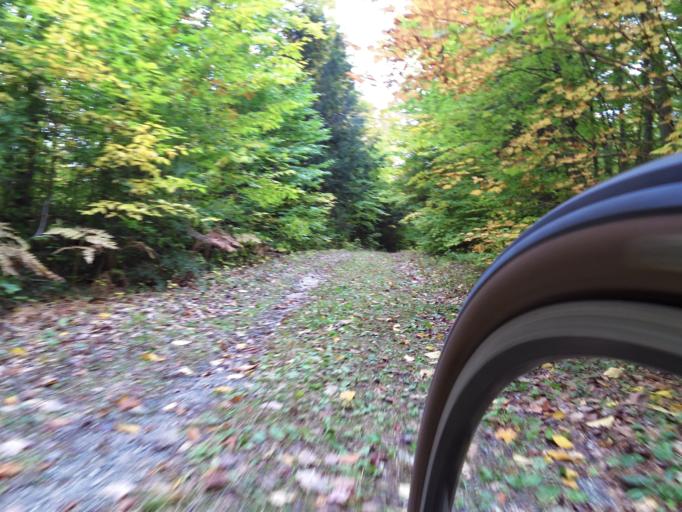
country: CA
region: Quebec
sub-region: Outaouais
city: Wakefield
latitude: 45.5979
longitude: -76.0677
